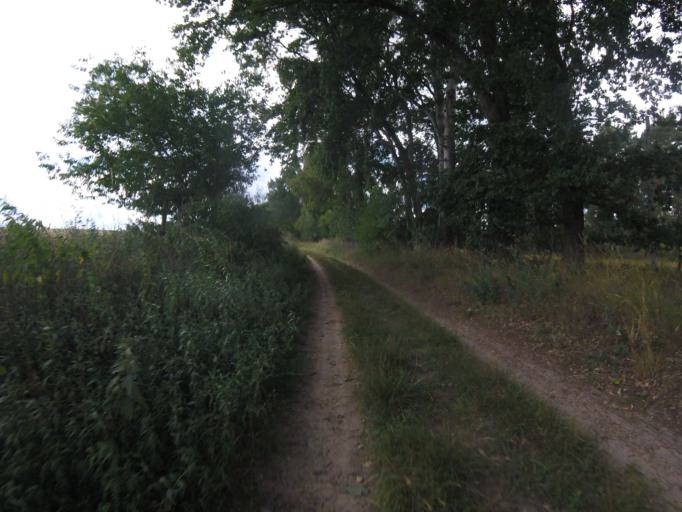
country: DE
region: Brandenburg
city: Mittenwalde
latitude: 52.2618
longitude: 13.5944
